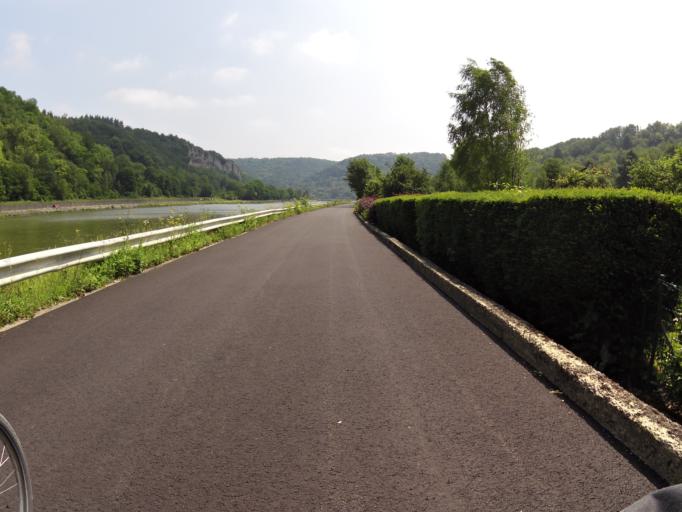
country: BE
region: Wallonia
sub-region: Province de Namur
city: Hastiere-Lavaux
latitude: 50.2105
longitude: 4.8470
